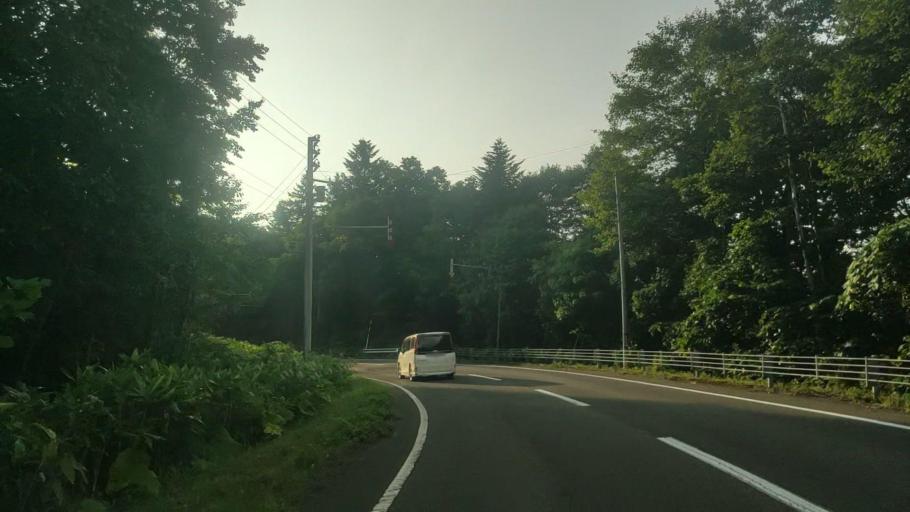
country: JP
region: Hokkaido
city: Bibai
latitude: 43.1738
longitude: 142.0704
